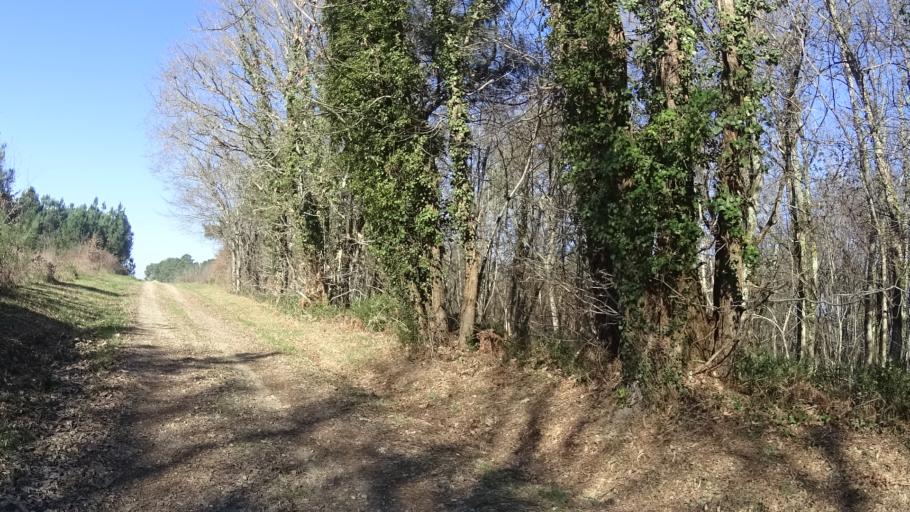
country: FR
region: Aquitaine
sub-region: Departement de la Dordogne
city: Saint-Medard-de-Mussidan
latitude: 45.0468
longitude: 0.2548
